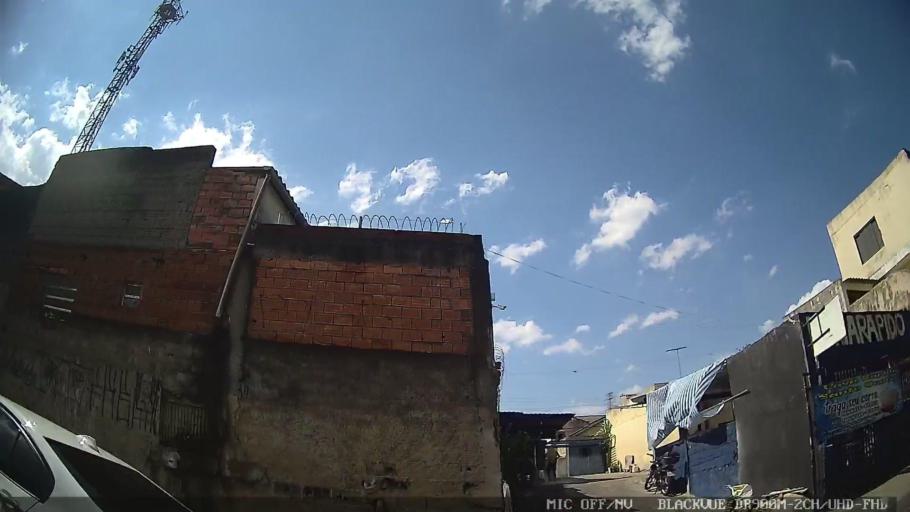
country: BR
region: Sao Paulo
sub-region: Guarulhos
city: Guarulhos
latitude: -23.5204
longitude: -46.5061
